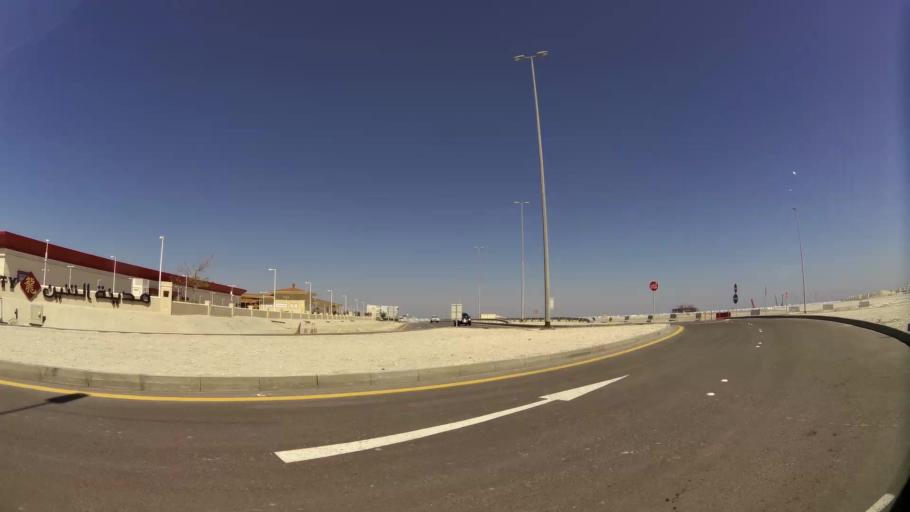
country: BH
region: Muharraq
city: Al Muharraq
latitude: 26.3035
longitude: 50.6265
